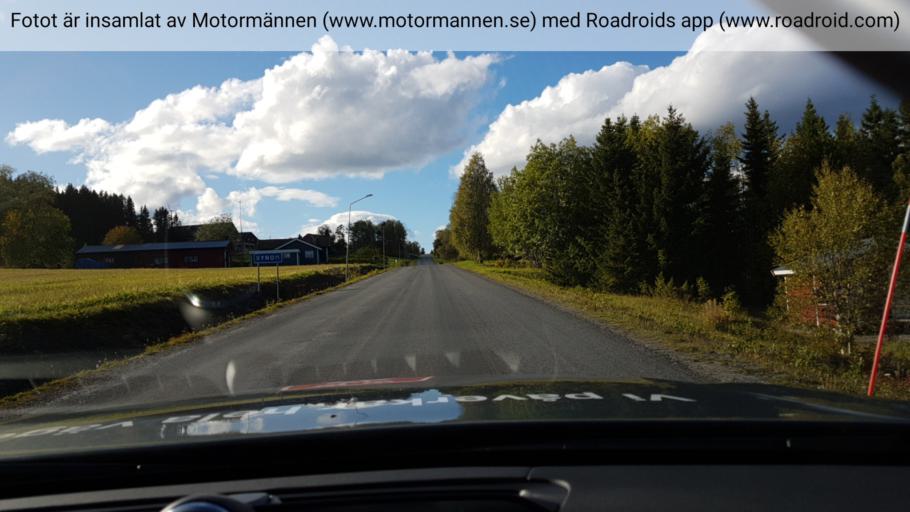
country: SE
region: Jaemtland
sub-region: Krokoms Kommun
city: Krokom
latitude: 63.1805
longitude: 14.0757
